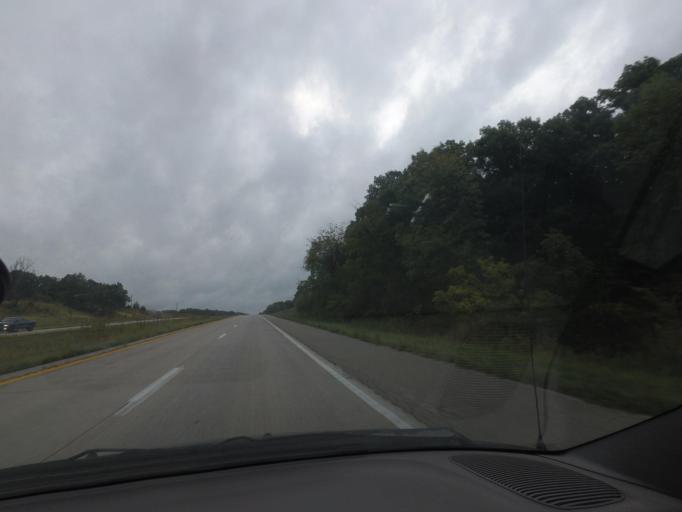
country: US
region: Missouri
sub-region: Shelby County
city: Shelbina
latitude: 39.6701
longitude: -91.8986
